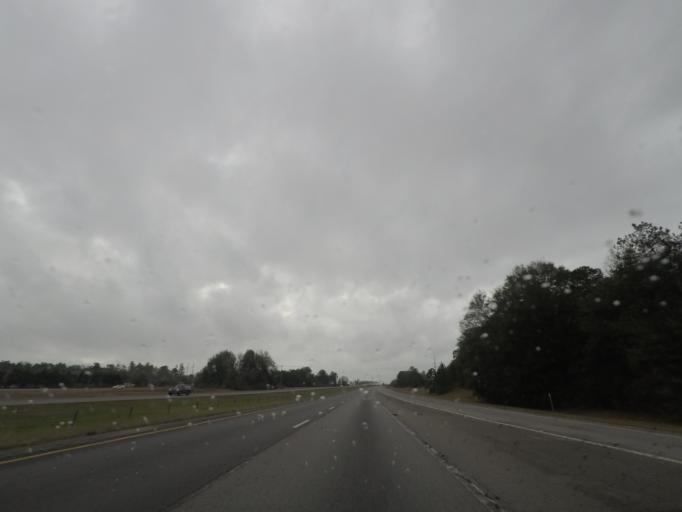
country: US
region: South Carolina
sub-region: Orangeburg County
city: Holly Hill
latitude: 33.5221
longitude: -80.4311
